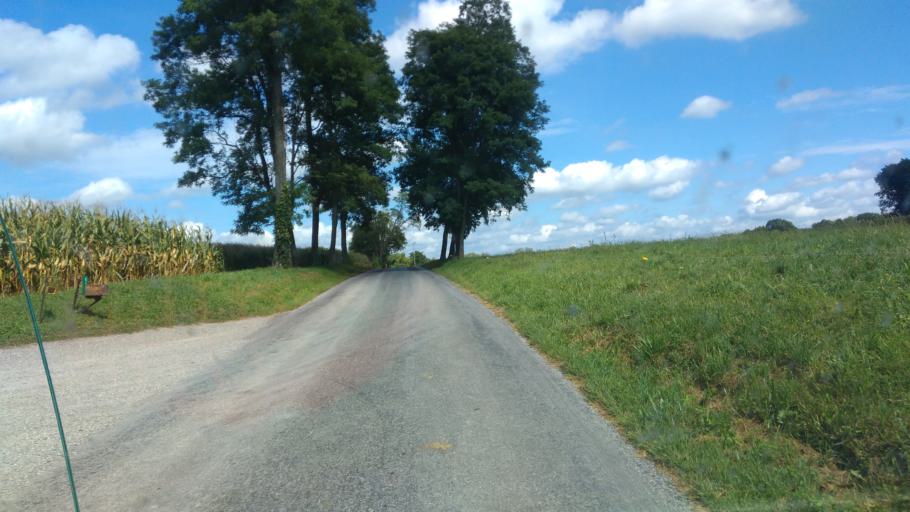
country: US
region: Ohio
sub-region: Holmes County
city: Millersburg
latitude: 40.6188
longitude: -81.8417
